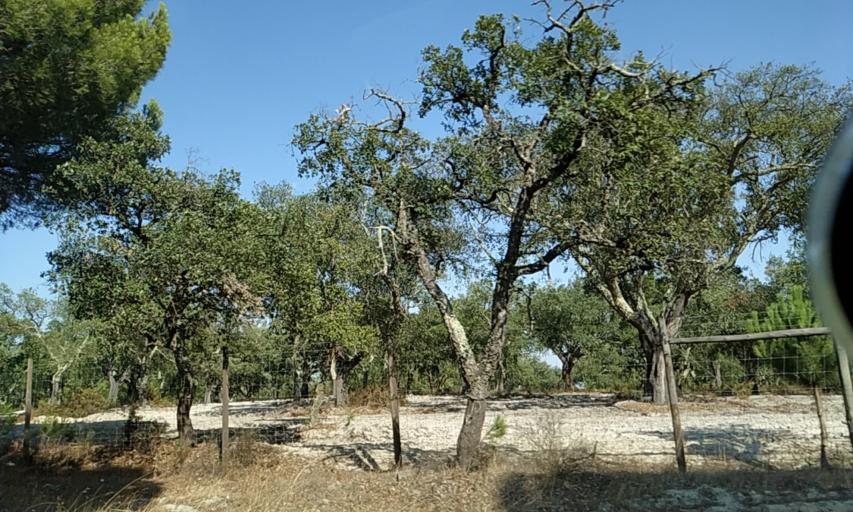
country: PT
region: Santarem
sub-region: Coruche
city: Coruche
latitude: 38.8142
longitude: -8.5746
